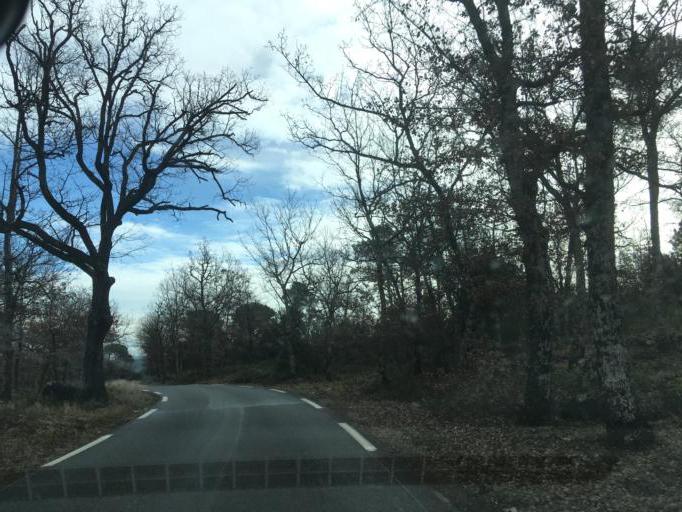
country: FR
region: Provence-Alpes-Cote d'Azur
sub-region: Departement du Var
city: Bras
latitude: 43.4482
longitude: 5.9898
